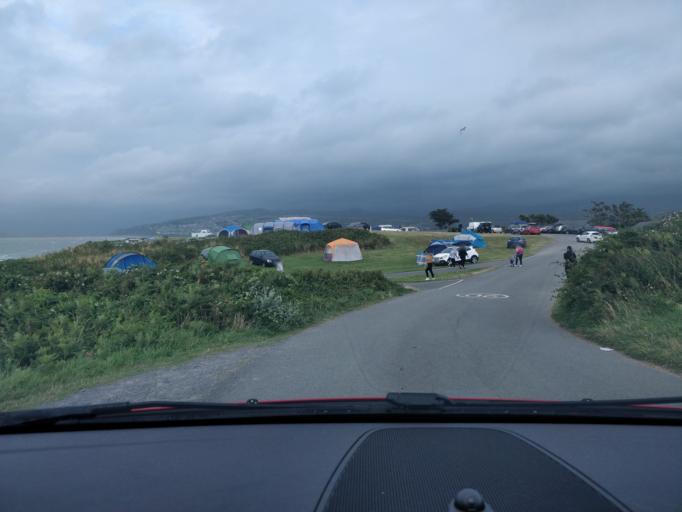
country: GB
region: Wales
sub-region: Gwynedd
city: Llanfair
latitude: 52.8179
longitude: -4.1462
